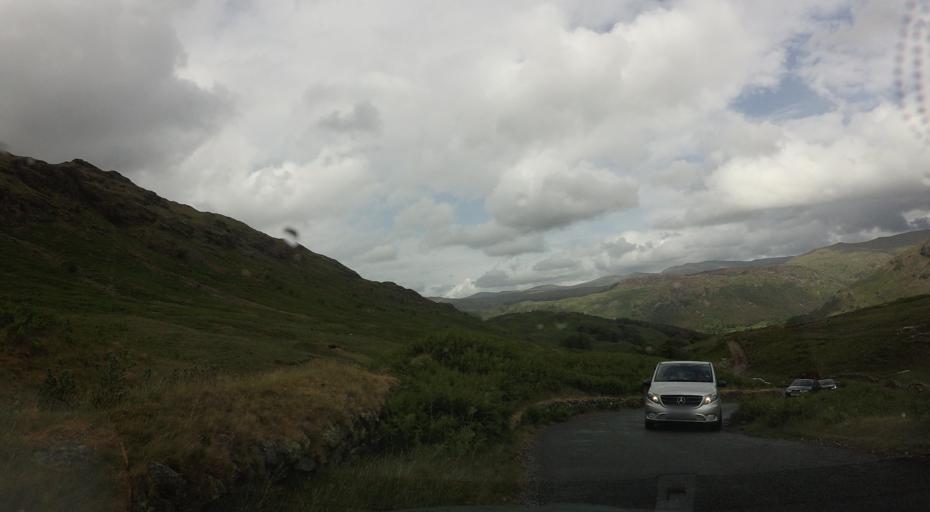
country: GB
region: England
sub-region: Cumbria
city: Keswick
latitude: 54.5138
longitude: -3.1840
